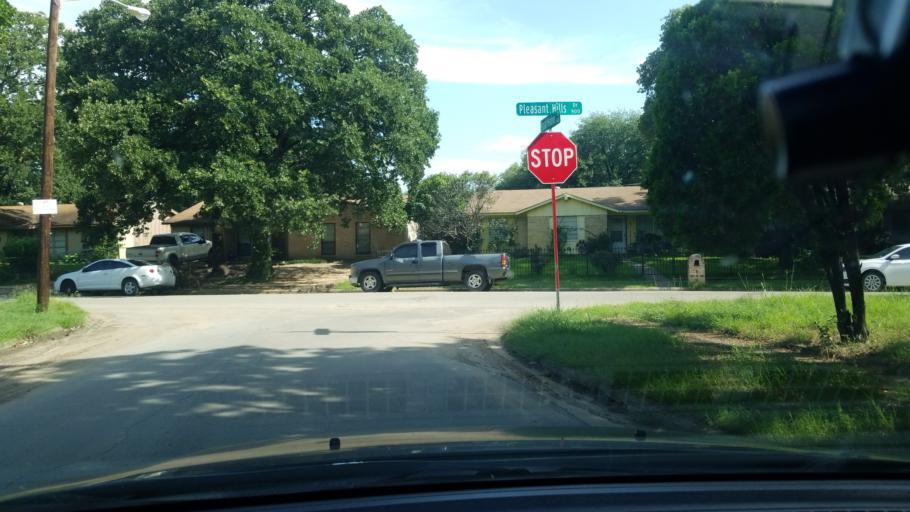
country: US
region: Texas
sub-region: Dallas County
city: Balch Springs
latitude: 32.7240
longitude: -96.6405
